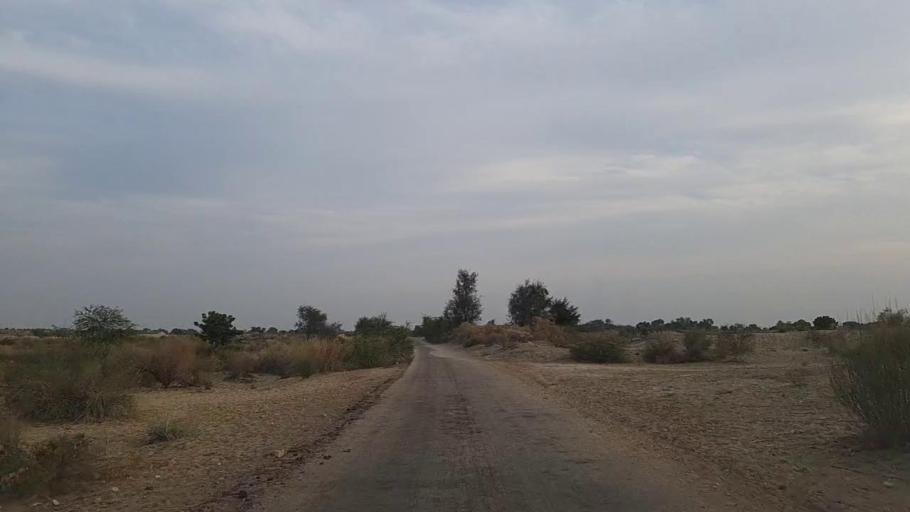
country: PK
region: Sindh
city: Jam Sahib
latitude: 26.4815
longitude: 68.5617
